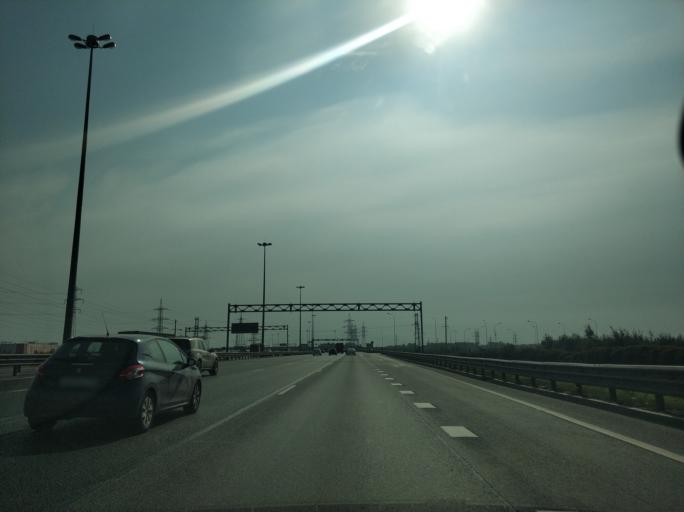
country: RU
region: Leningrad
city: Murino
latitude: 60.0228
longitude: 30.4529
